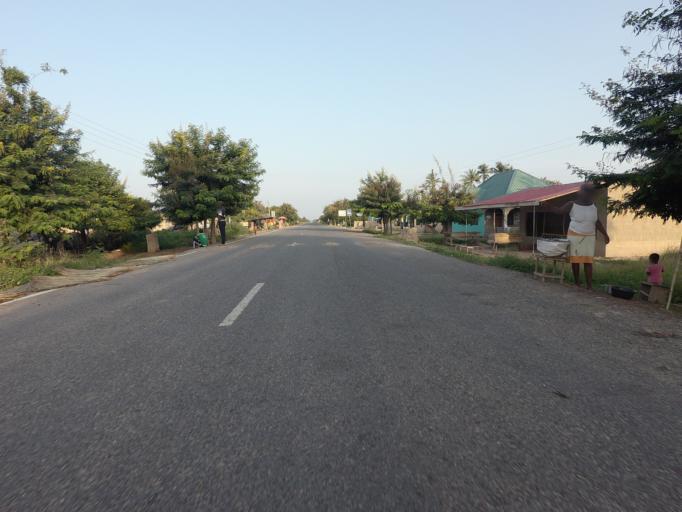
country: GH
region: Volta
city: Anloga
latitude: 5.8928
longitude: 0.7174
